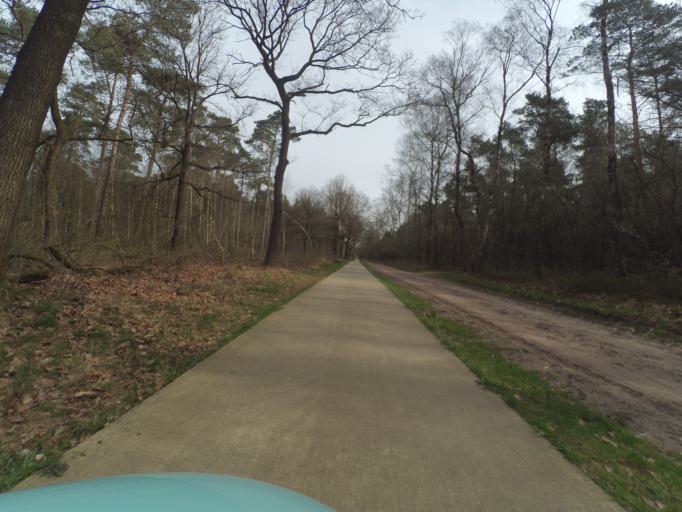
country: NL
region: Gelderland
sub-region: Gemeente Ede
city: Otterlo
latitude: 52.0904
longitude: 5.7565
